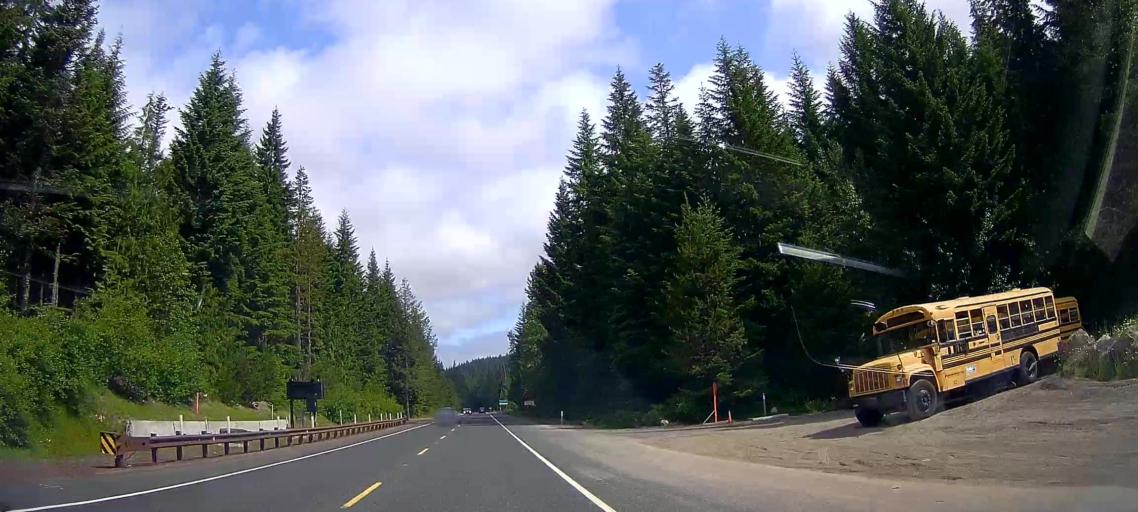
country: US
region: Oregon
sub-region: Clackamas County
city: Mount Hood Village
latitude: 45.2527
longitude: -121.7110
